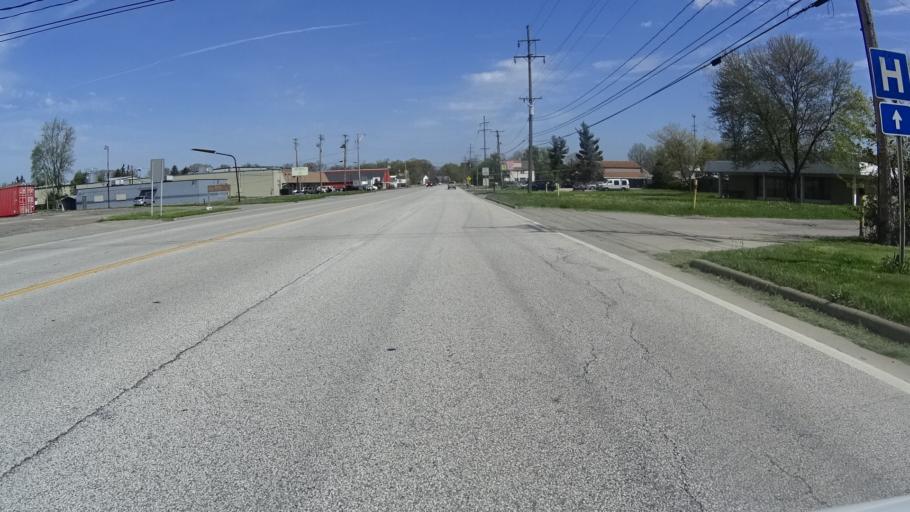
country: US
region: Ohio
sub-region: Lorain County
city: Elyria
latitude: 41.3386
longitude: -82.1173
